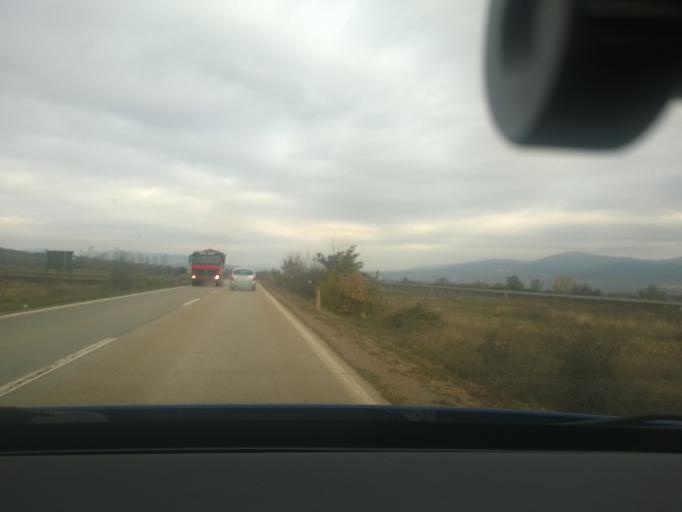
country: RS
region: Central Serbia
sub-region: Pirotski Okrug
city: Pirot
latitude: 43.0756
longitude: 22.6679
